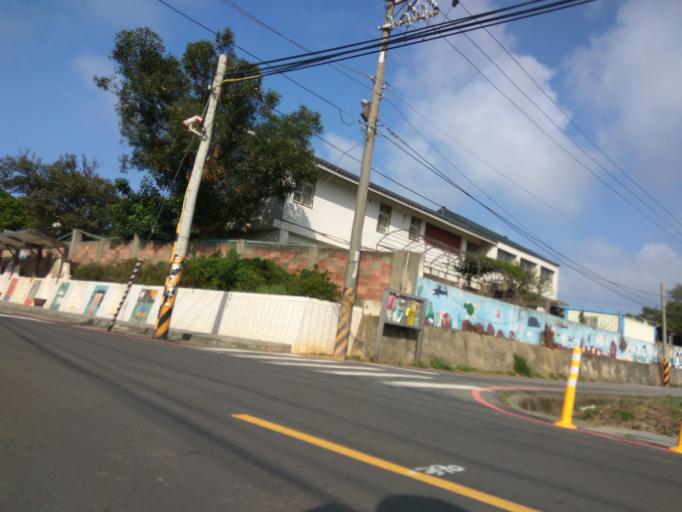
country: TW
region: Taiwan
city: Taoyuan City
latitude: 25.0647
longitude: 121.1726
